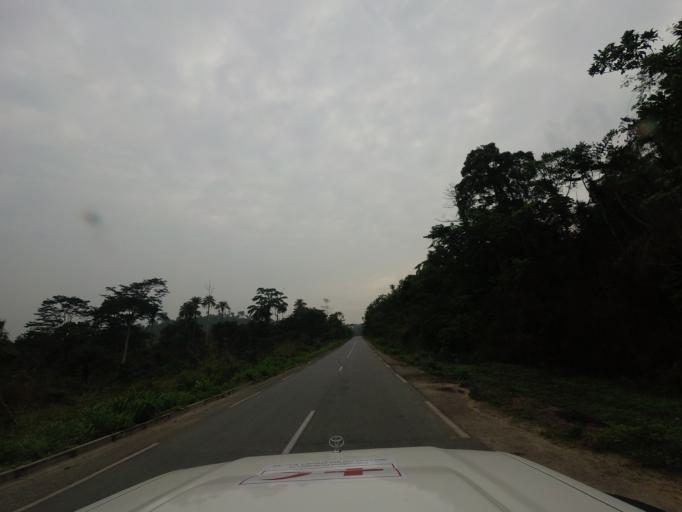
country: LR
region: Lofa
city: Voinjama
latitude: 8.6199
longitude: -9.7478
